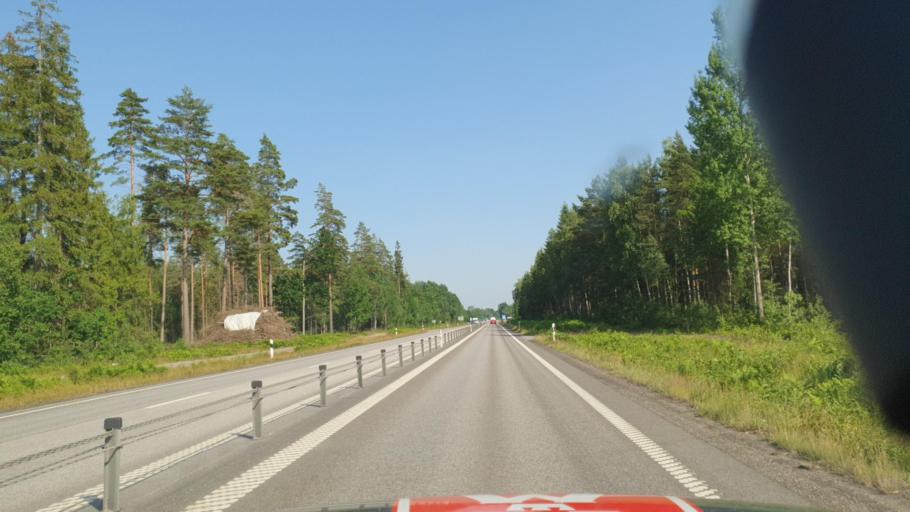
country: SE
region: Kalmar
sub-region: Kalmar Kommun
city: Trekanten
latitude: 56.7100
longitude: 16.0736
